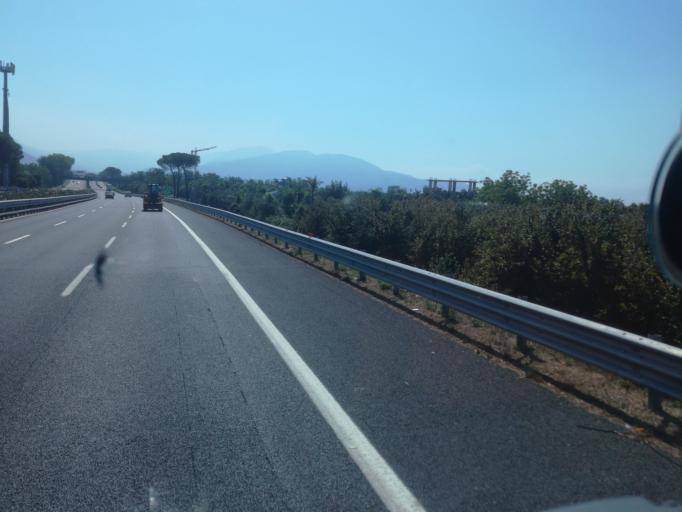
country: IT
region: Campania
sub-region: Provincia di Napoli
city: Saviano
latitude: 40.9198
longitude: 14.5089
